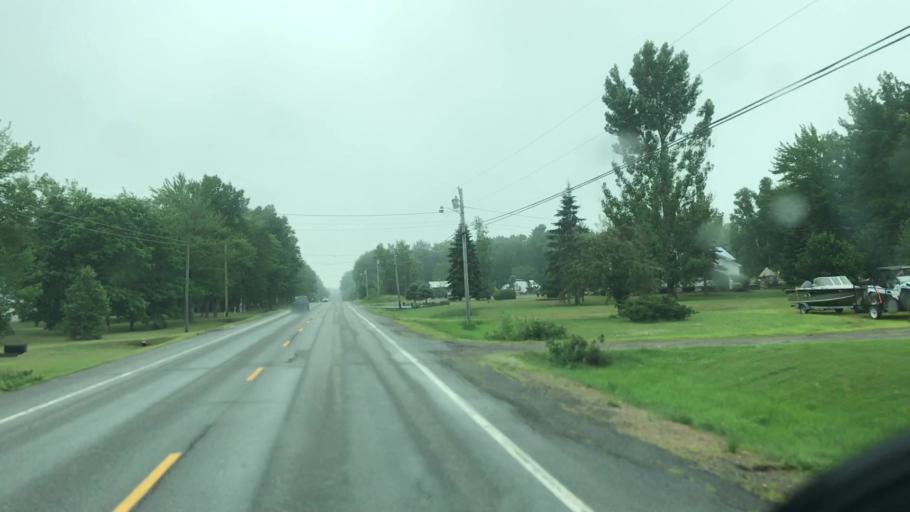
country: US
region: Maine
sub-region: Penobscot County
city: Howland
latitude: 45.2668
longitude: -68.6387
